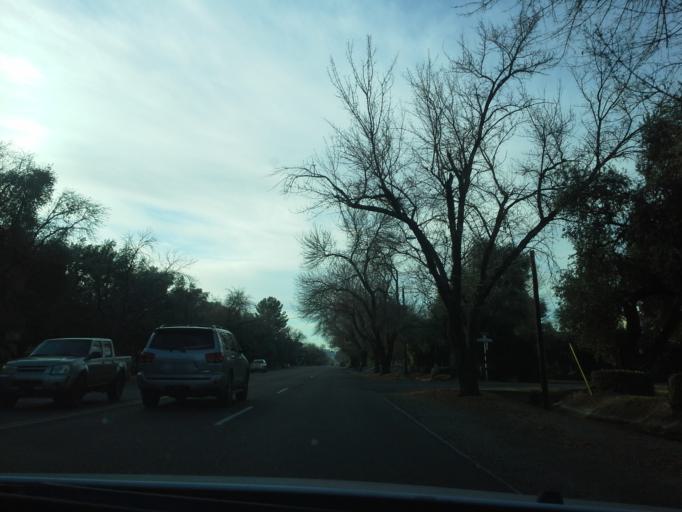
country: US
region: Arizona
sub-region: Maricopa County
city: Phoenix
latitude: 33.5336
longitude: -112.0738
